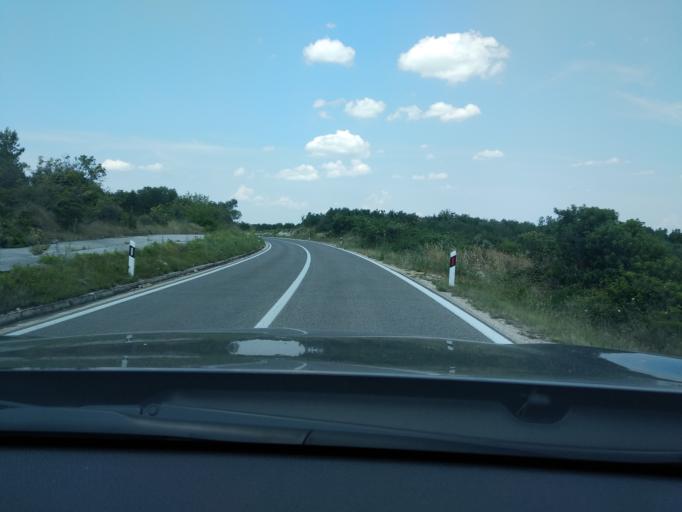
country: HR
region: Sibensko-Kniniska
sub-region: Grad Sibenik
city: Pirovac
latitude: 43.8036
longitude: 15.6643
